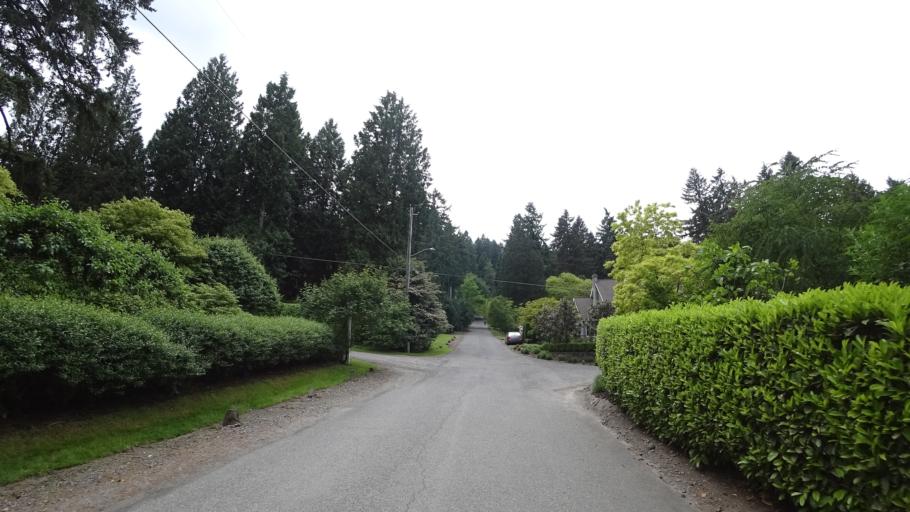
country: US
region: Oregon
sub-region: Clackamas County
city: Milwaukie
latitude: 45.4505
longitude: -122.6616
